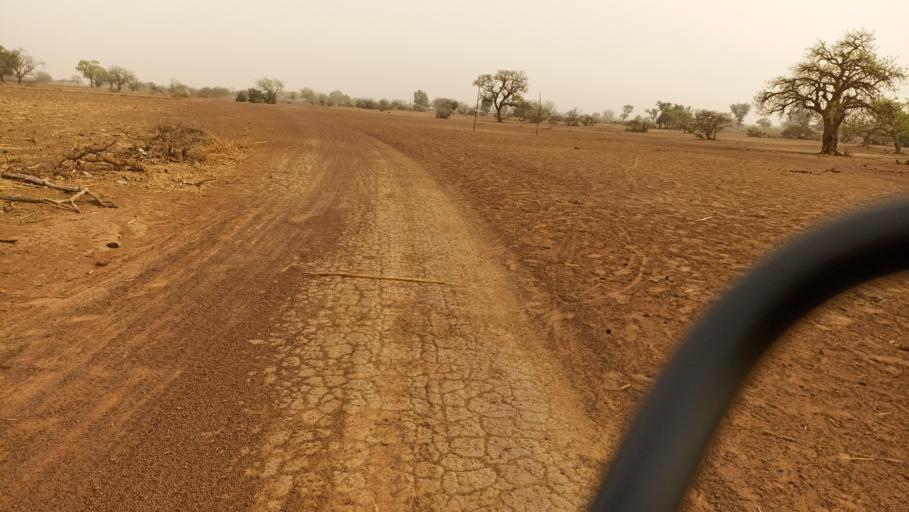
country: BF
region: Nord
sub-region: Province du Zondoma
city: Gourcy
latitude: 13.1427
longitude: -2.5973
